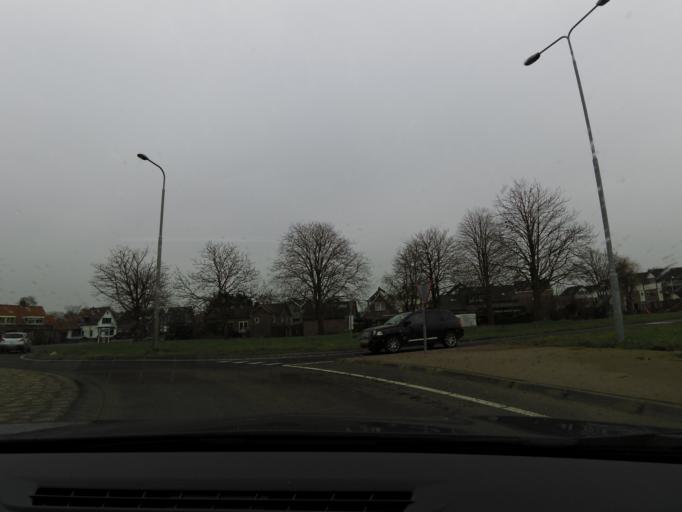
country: NL
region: South Holland
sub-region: Gemeente Nieuwkoop
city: Nieuwkoop
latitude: 52.1550
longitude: 4.7819
